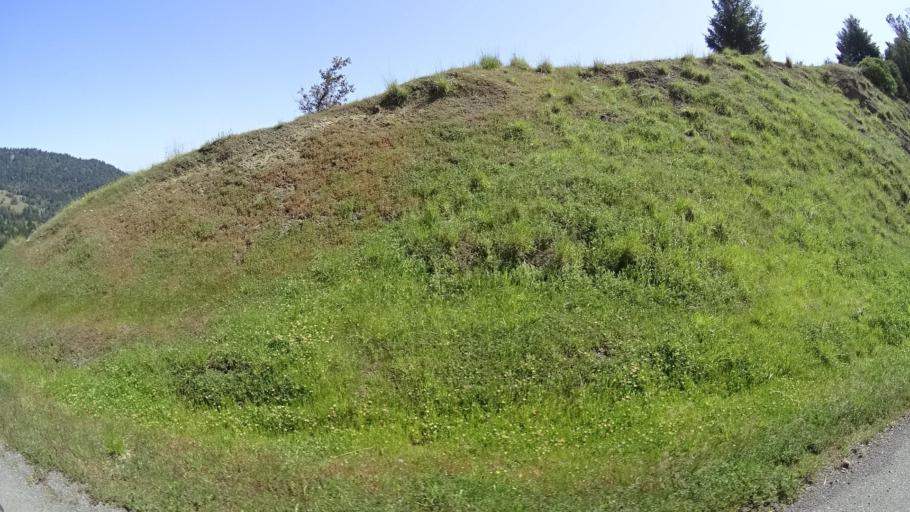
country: US
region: California
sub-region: Humboldt County
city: Redway
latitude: 40.1093
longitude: -123.6701
